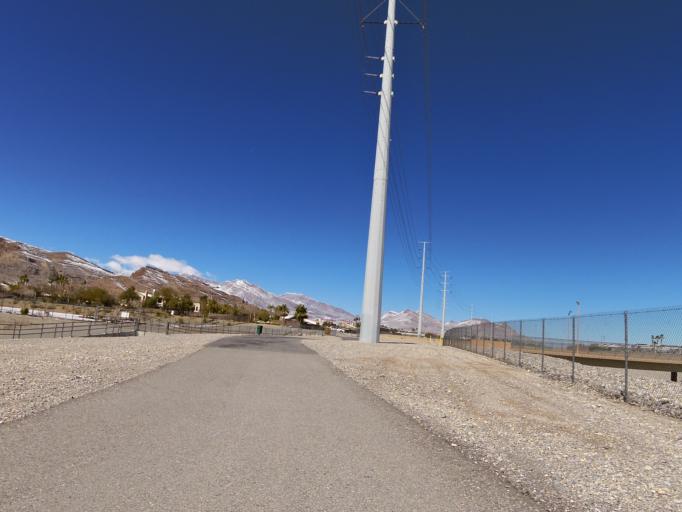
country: US
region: Nevada
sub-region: Clark County
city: Summerlin South
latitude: 36.1285
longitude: -115.3350
